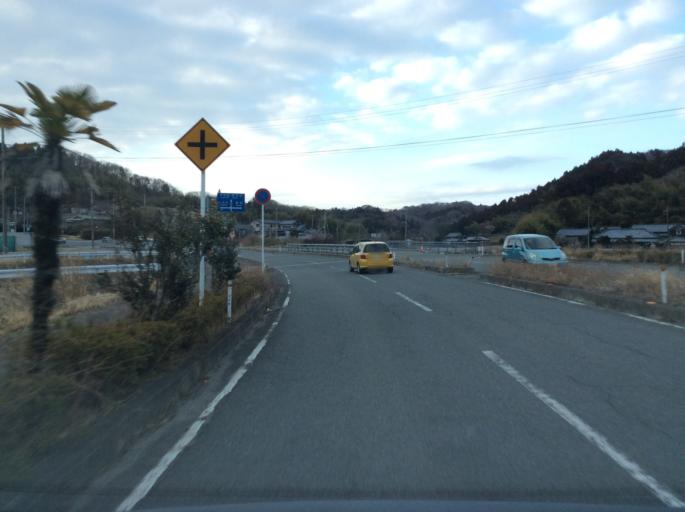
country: JP
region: Fukushima
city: Iwaki
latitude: 36.9692
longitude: 140.9186
